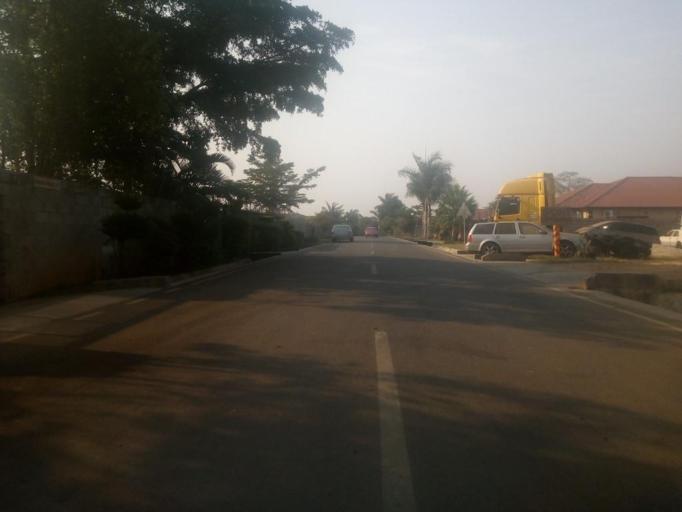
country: ZM
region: Lusaka
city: Lusaka
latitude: -15.3997
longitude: 28.3853
